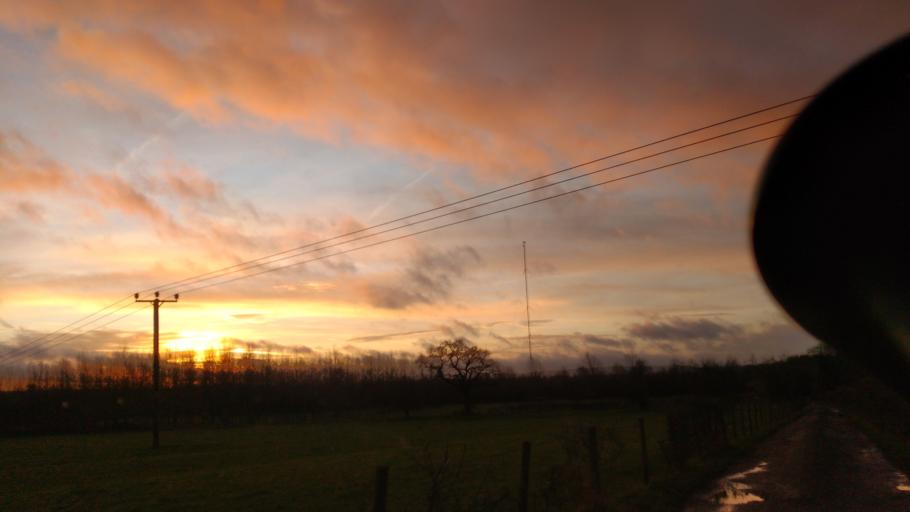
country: GB
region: England
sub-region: Borough of Swindon
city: Highworth
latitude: 51.5961
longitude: -1.6964
